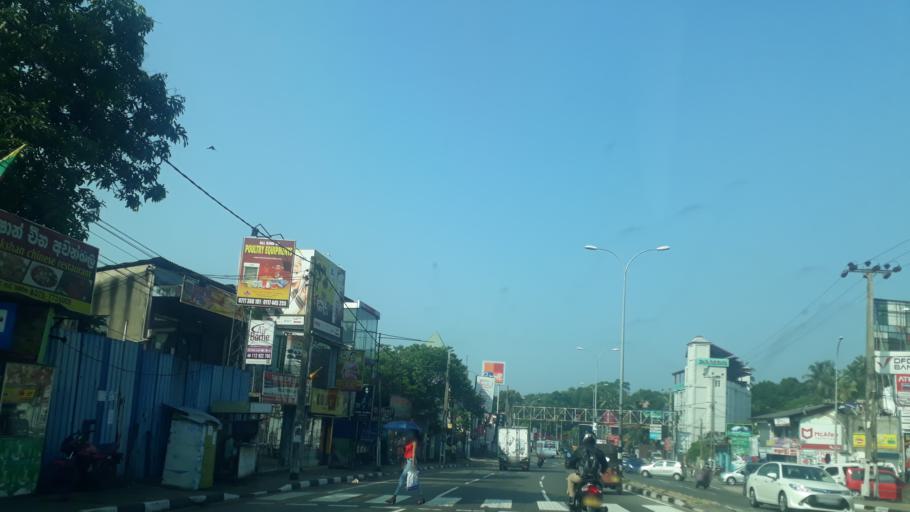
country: LK
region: Western
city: Kelaniya
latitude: 7.0010
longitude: 79.9499
